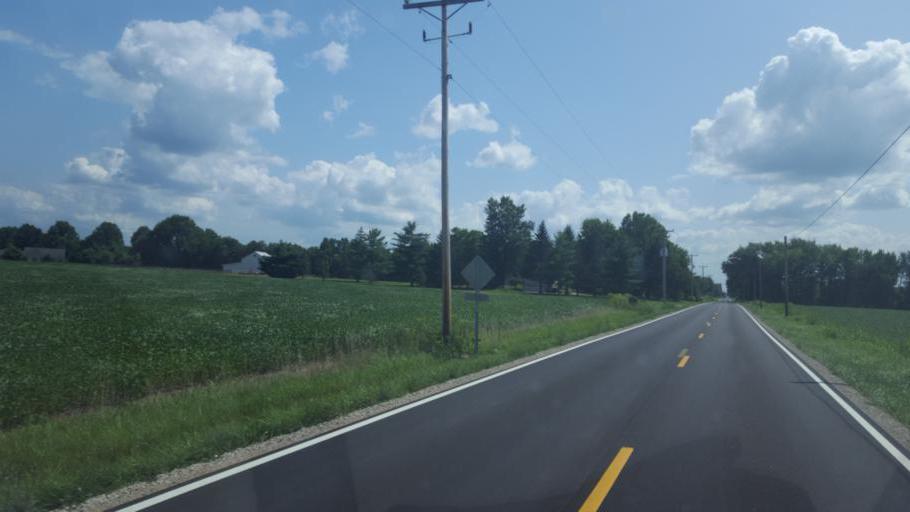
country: US
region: Ohio
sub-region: Delaware County
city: Sunbury
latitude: 40.3095
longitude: -82.9129
